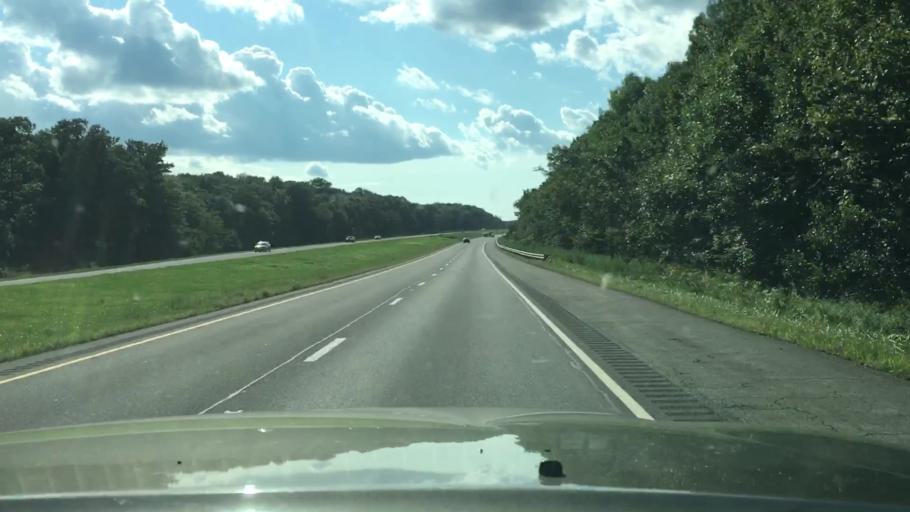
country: US
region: Pennsylvania
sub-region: Wayne County
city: Hawley
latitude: 41.3597
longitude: -75.1869
